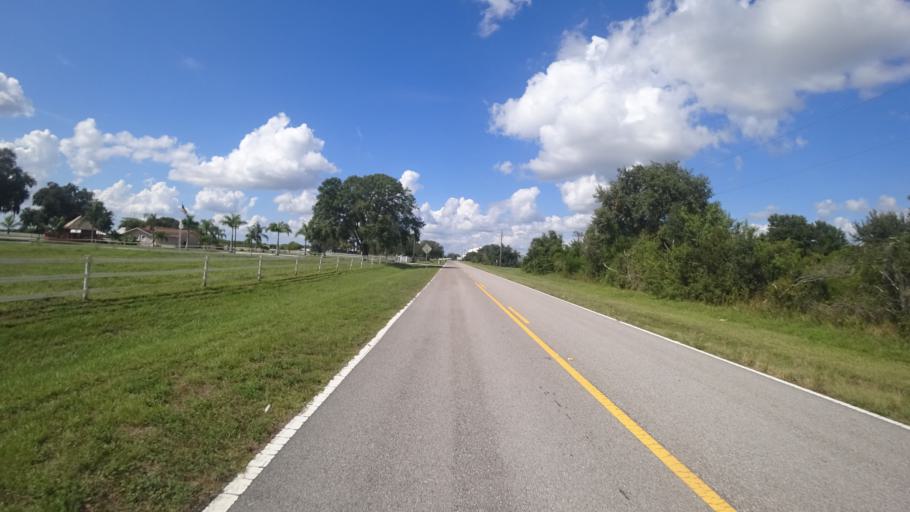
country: US
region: Florida
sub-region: Sarasota County
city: The Meadows
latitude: 27.4847
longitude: -82.3528
